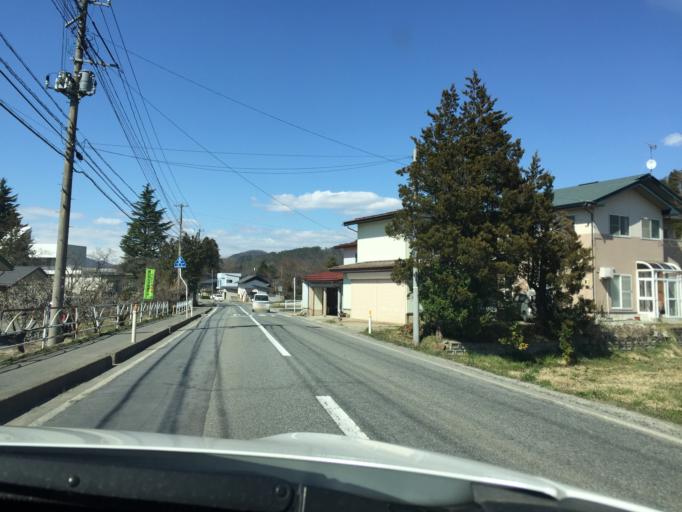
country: JP
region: Yamagata
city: Nagai
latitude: 38.1917
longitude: 140.1010
